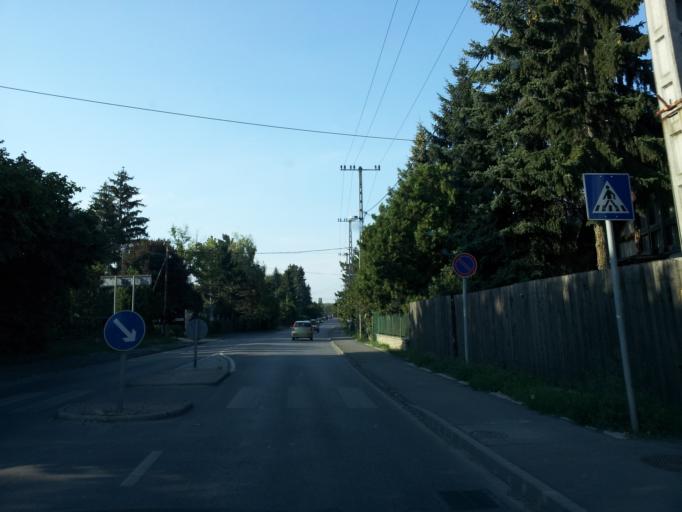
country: HU
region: Pest
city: Leanyfalu
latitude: 47.6946
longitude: 19.0884
